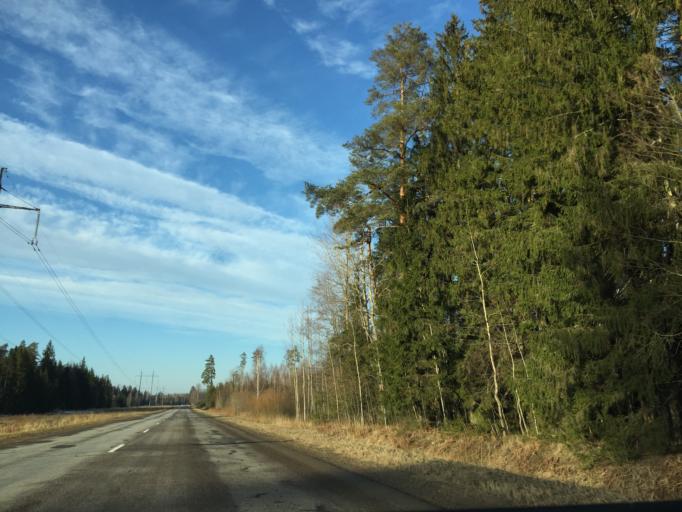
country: LV
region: Kekava
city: Balozi
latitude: 56.7903
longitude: 24.0759
